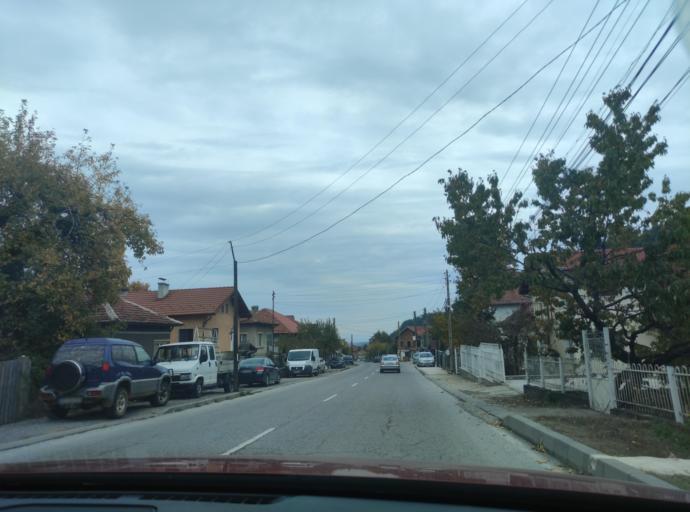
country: BG
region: Montana
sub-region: Obshtina Berkovitsa
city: Berkovitsa
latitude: 43.1909
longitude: 23.1595
